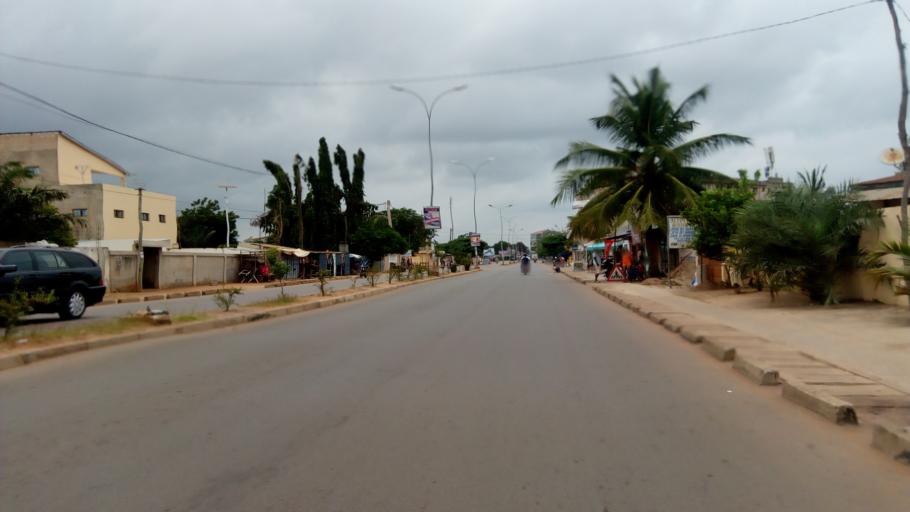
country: TG
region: Maritime
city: Lome
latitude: 6.2188
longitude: 1.2042
